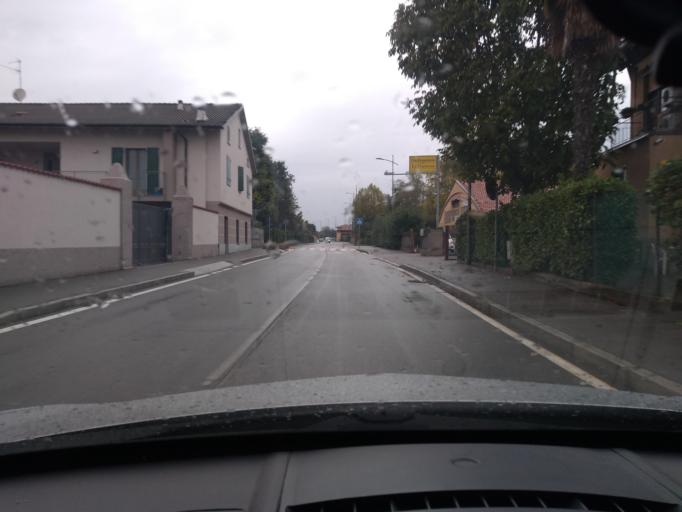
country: IT
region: Lombardy
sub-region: Provincia di Bergamo
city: Mornico al Serio
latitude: 45.5948
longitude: 9.8091
